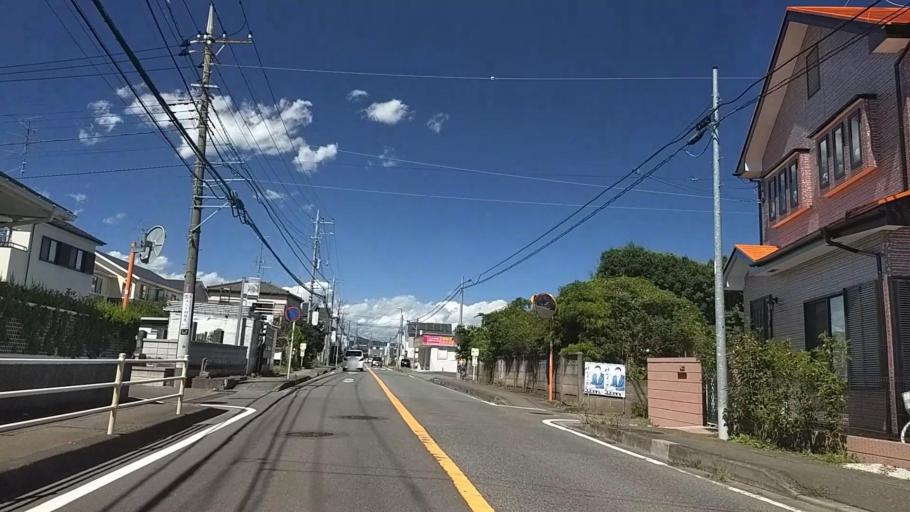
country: JP
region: Tokyo
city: Hachioji
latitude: 35.5742
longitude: 139.3172
